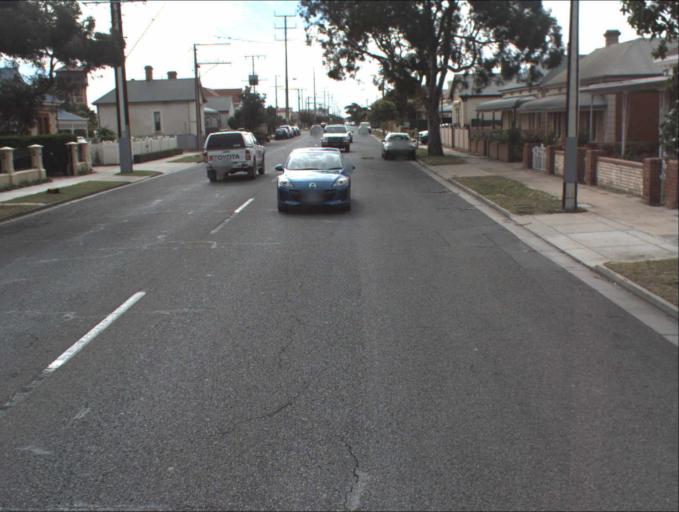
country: AU
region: South Australia
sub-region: Port Adelaide Enfield
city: Birkenhead
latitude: -34.8432
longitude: 138.4823
